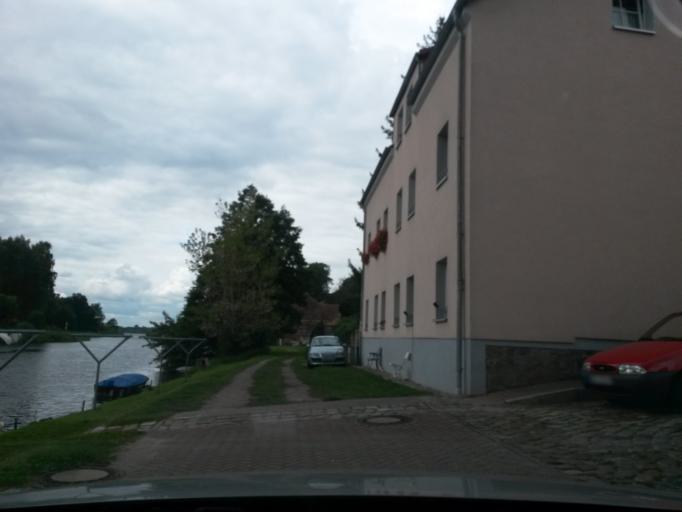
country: DE
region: Brandenburg
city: Oderberg
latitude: 52.8647
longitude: 14.0398
